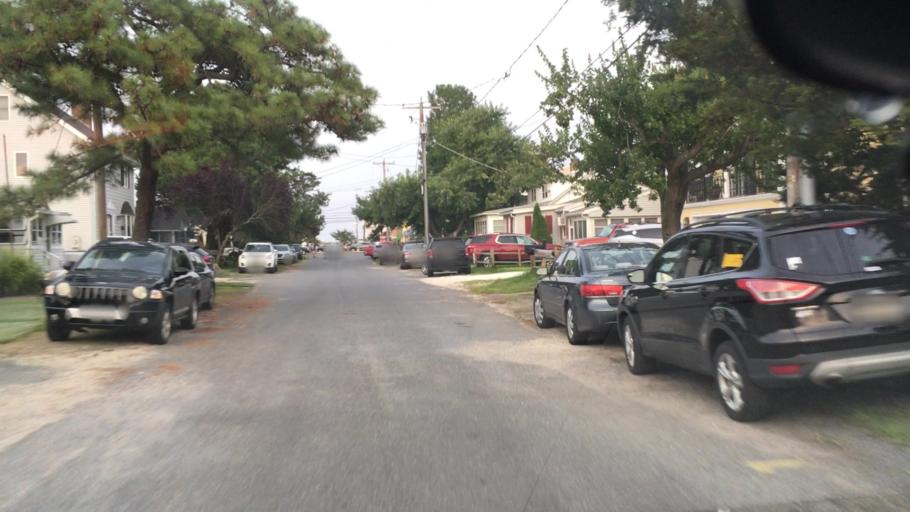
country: US
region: Delaware
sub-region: Sussex County
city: Rehoboth Beach
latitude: 38.6950
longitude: -75.0768
